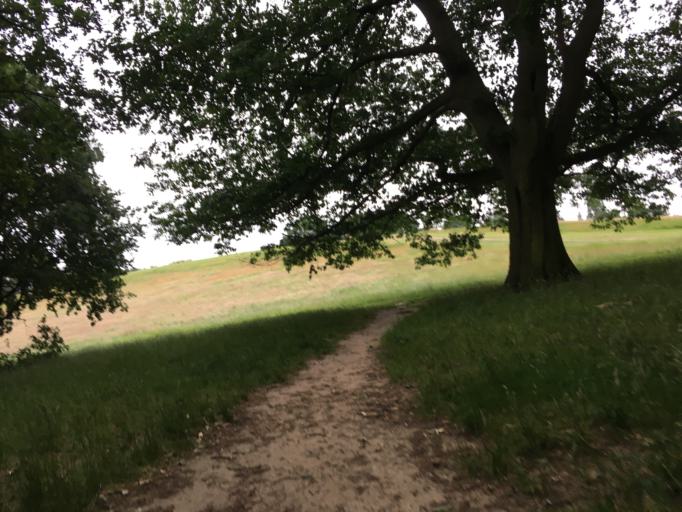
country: GB
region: England
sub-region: Greater London
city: Belsize Park
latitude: 51.5609
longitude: -0.1603
